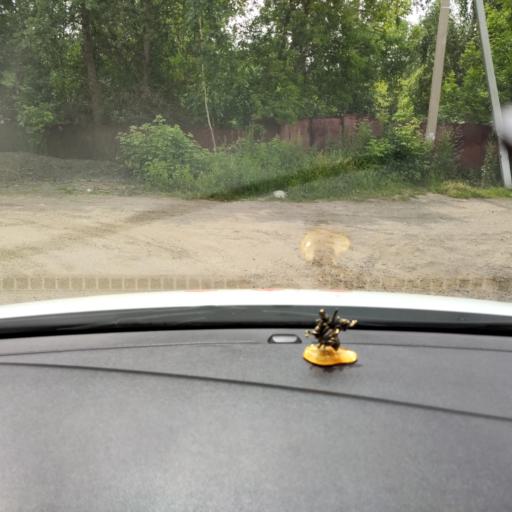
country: RU
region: Tatarstan
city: Staroye Arakchino
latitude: 55.8902
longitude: 49.0420
